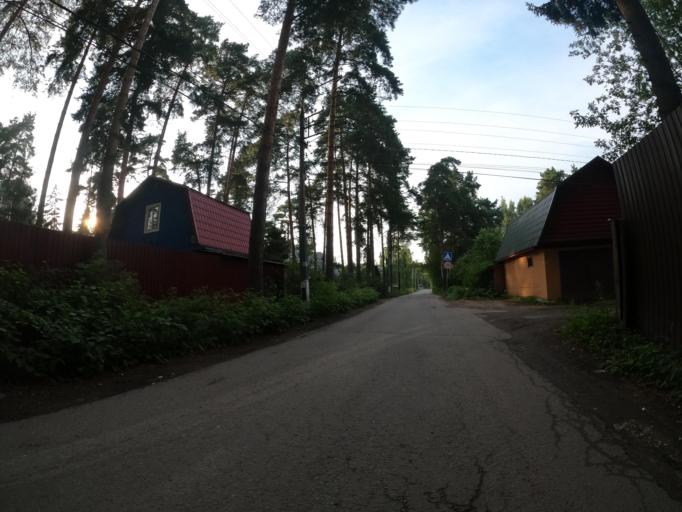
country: RU
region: Moskovskaya
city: Bykovo
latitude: 55.6383
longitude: 38.0991
